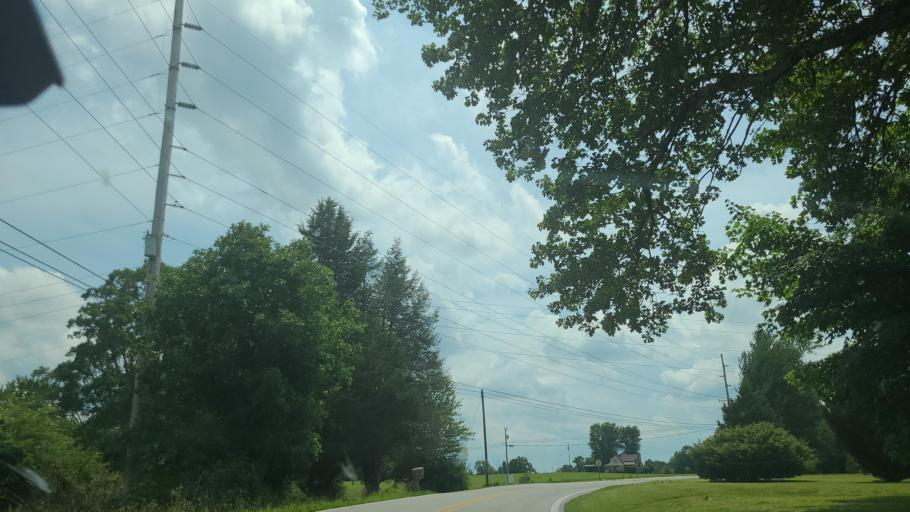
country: US
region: Tennessee
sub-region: Cumberland County
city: Crossville
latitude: 35.9074
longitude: -85.0271
